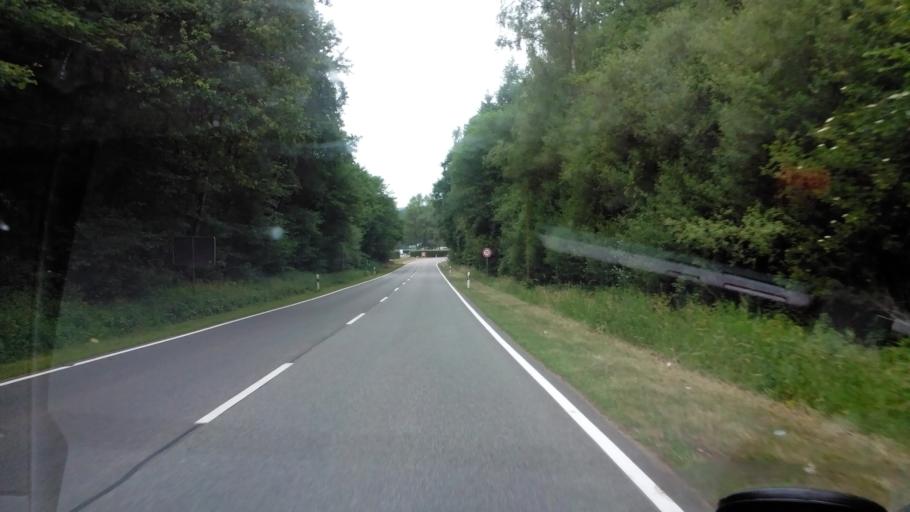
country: DE
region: Saarland
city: Mettlach
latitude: 49.4911
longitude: 6.6287
